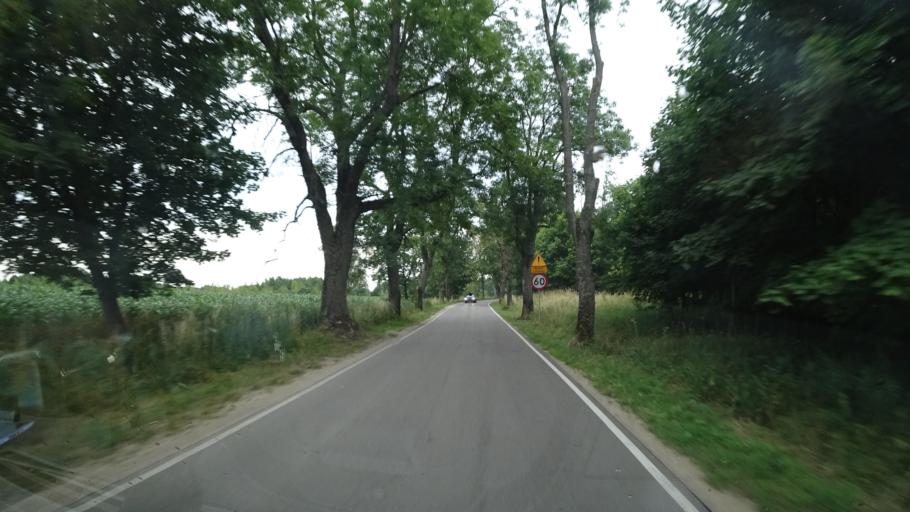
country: PL
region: Warmian-Masurian Voivodeship
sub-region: Powiat gizycki
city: Ryn
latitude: 53.8764
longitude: 21.5891
